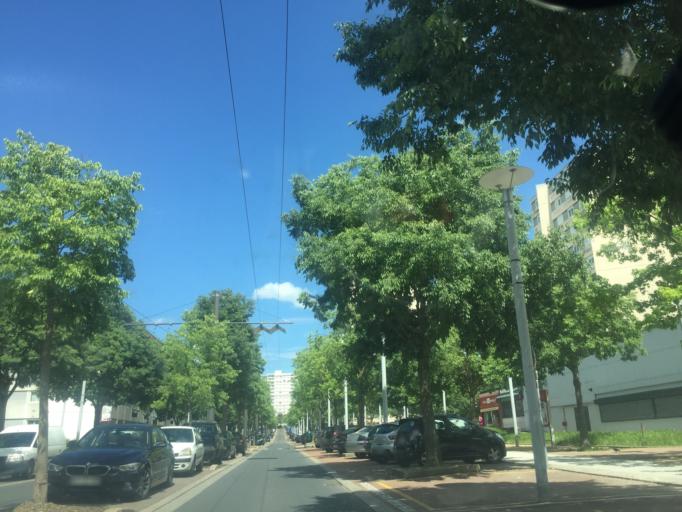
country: FR
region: Rhone-Alpes
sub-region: Departement du Rhone
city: Rillieux-la-Pape
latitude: 45.8145
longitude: 4.8943
